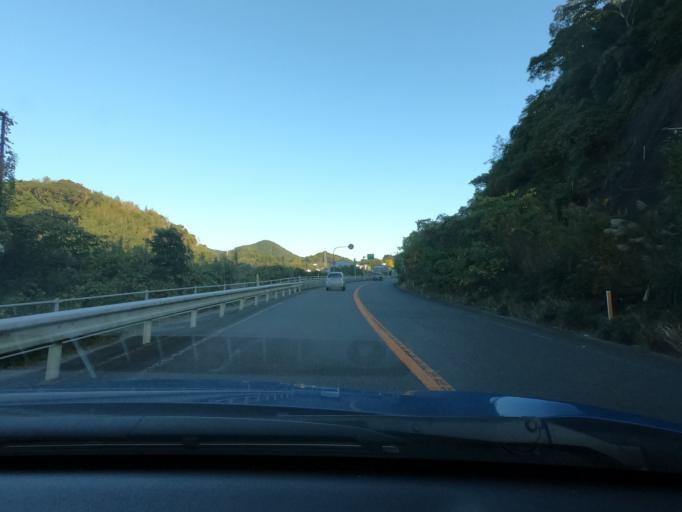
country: JP
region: Kagoshima
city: Satsumasendai
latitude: 31.8512
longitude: 130.2396
